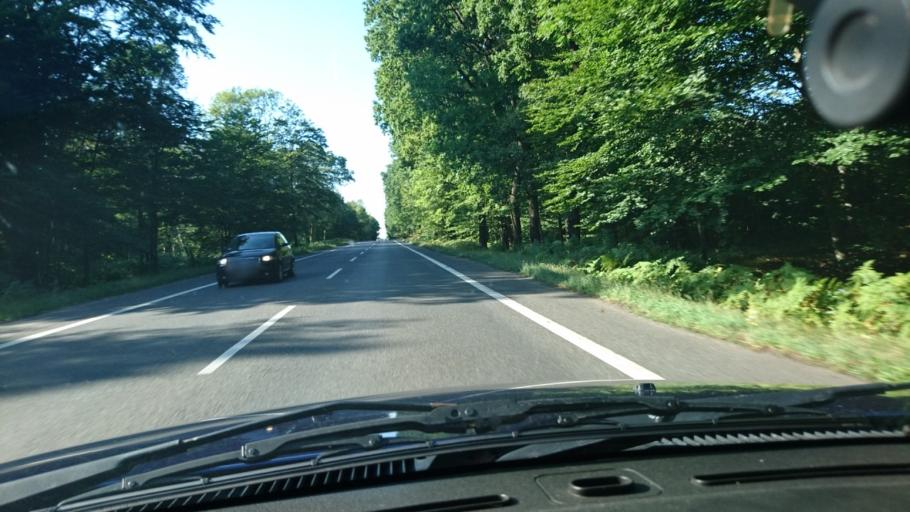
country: PL
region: Silesian Voivodeship
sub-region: Powiat gliwicki
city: Pyskowice
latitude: 50.3468
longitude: 18.6491
